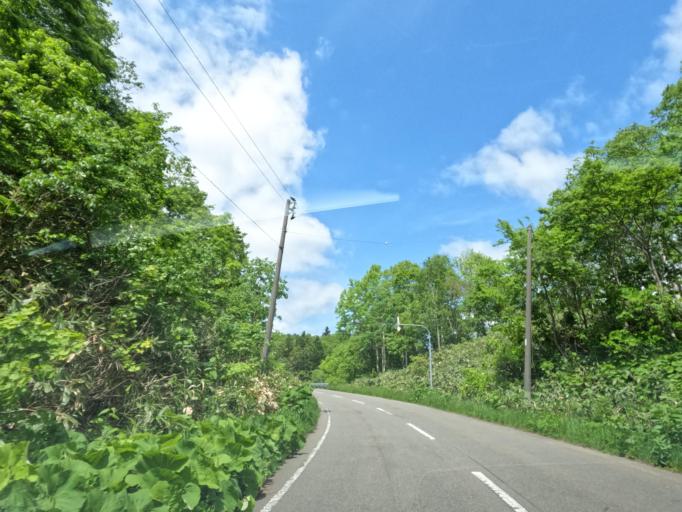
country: JP
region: Hokkaido
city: Sunagawa
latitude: 43.5065
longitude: 141.6078
